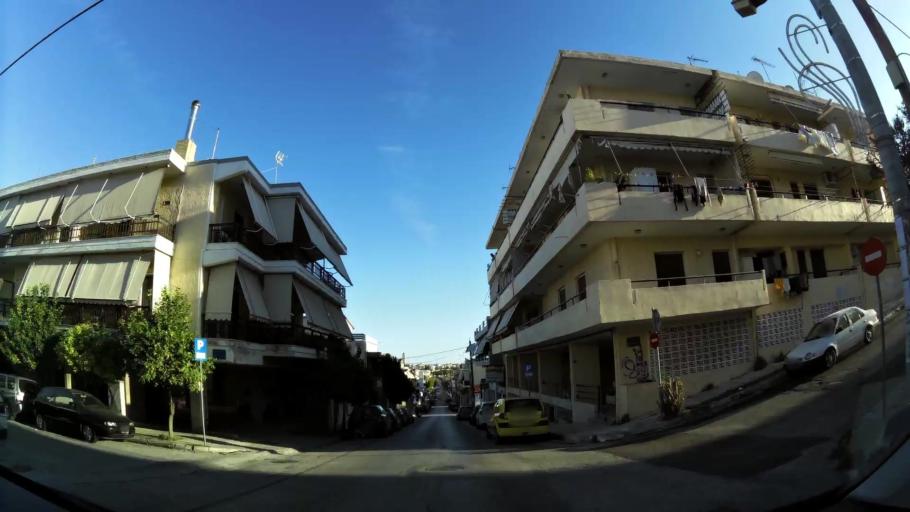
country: GR
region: Attica
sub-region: Nomarchia Anatolikis Attikis
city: Rafina
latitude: 38.0225
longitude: 24.0054
